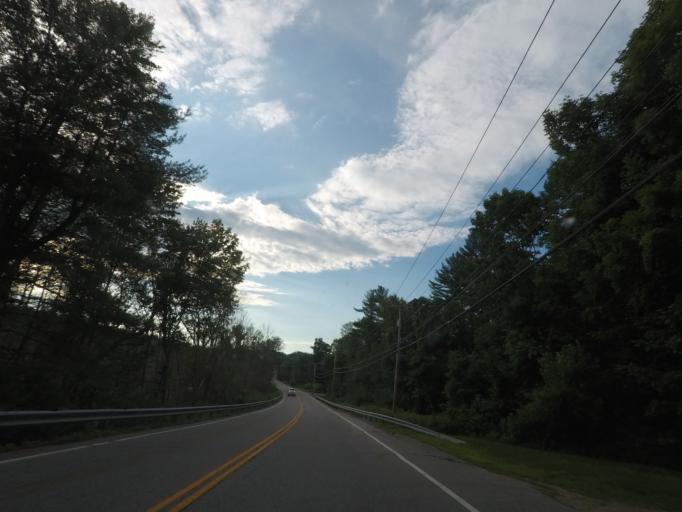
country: US
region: Connecticut
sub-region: Windham County
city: North Grosvenor Dale
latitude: 41.9966
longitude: -71.9006
